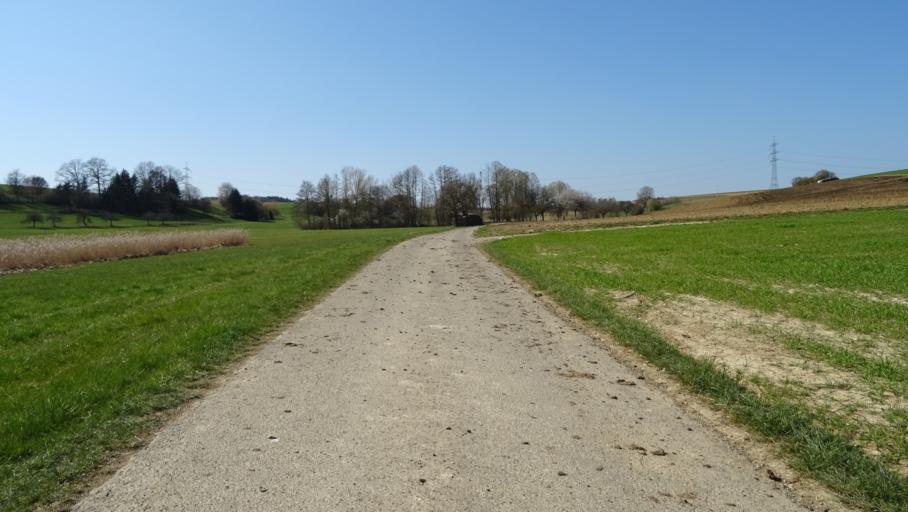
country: DE
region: Baden-Wuerttemberg
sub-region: Karlsruhe Region
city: Billigheim
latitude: 49.4014
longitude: 9.2692
